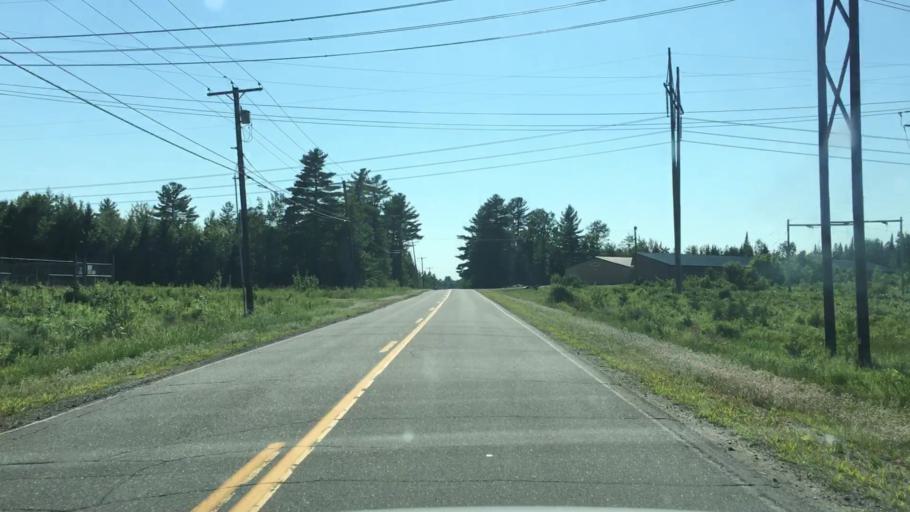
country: US
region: Maine
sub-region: Penobscot County
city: Enfield
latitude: 45.2462
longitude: -68.6014
